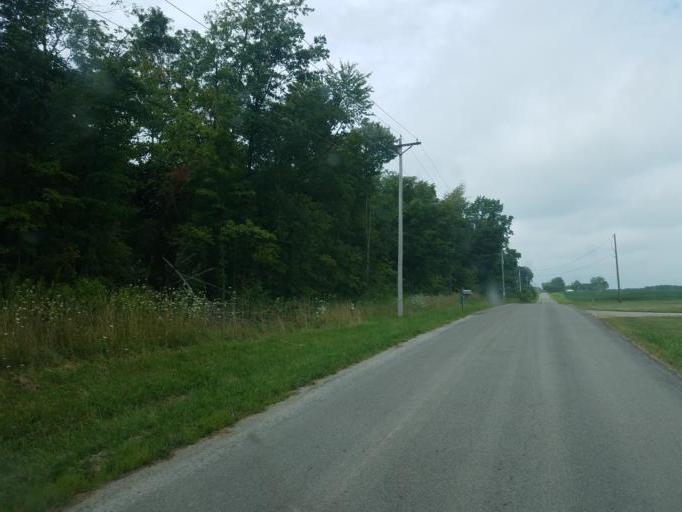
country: US
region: Ohio
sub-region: Morrow County
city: Mount Gilead
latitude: 40.4751
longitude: -82.7616
